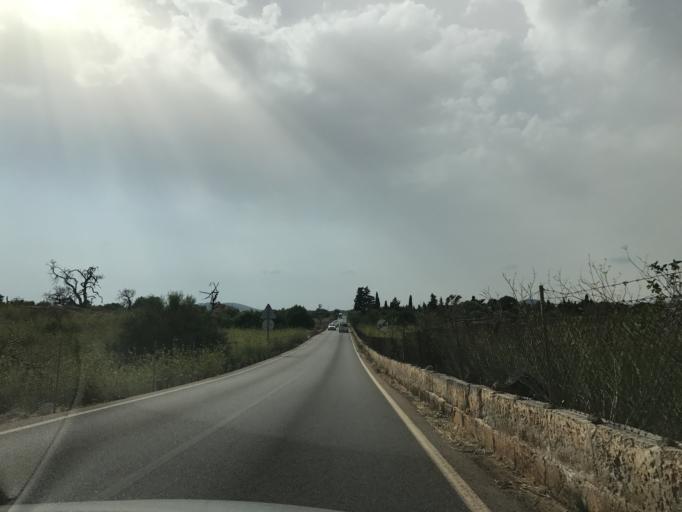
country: ES
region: Balearic Islands
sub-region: Illes Balears
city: Son Servera
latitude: 39.5700
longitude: 3.3637
